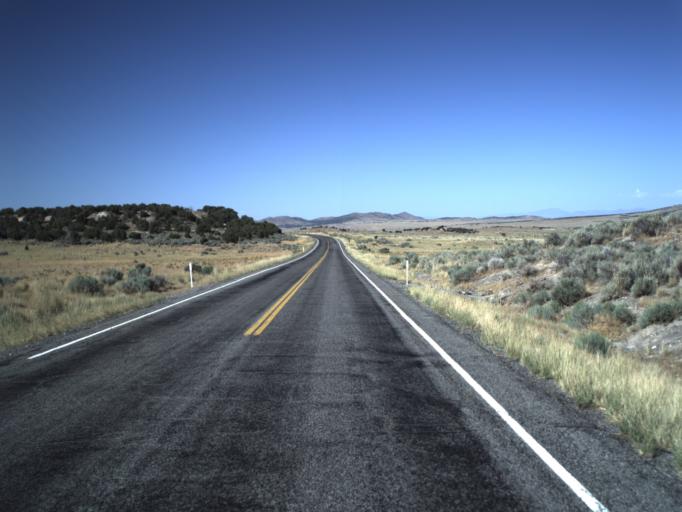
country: US
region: Utah
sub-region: Juab County
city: Mona
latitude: 39.7643
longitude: -112.1713
